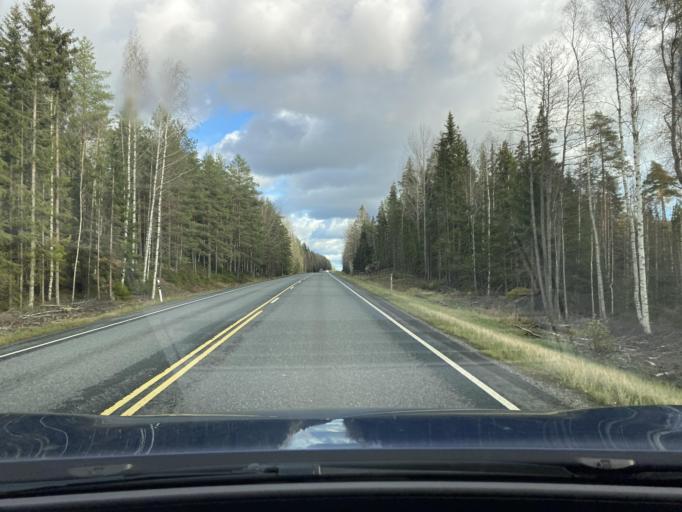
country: FI
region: Haeme
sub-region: Forssa
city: Humppila
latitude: 60.9357
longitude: 23.2603
